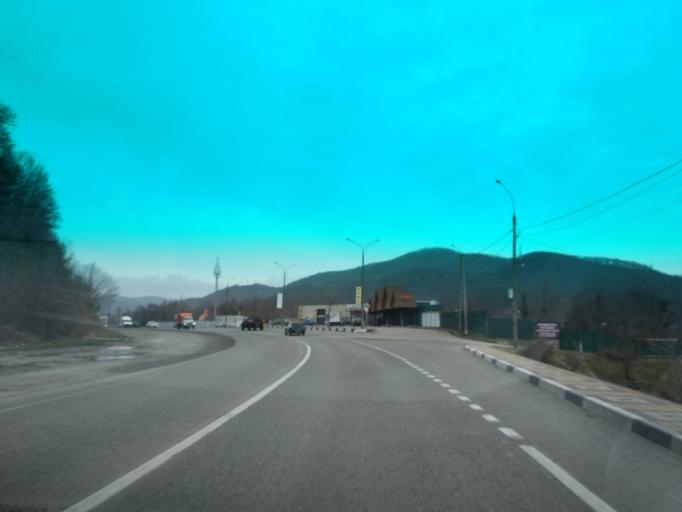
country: RU
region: Krasnodarskiy
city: Ol'ginka
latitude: 44.2132
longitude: 38.8945
